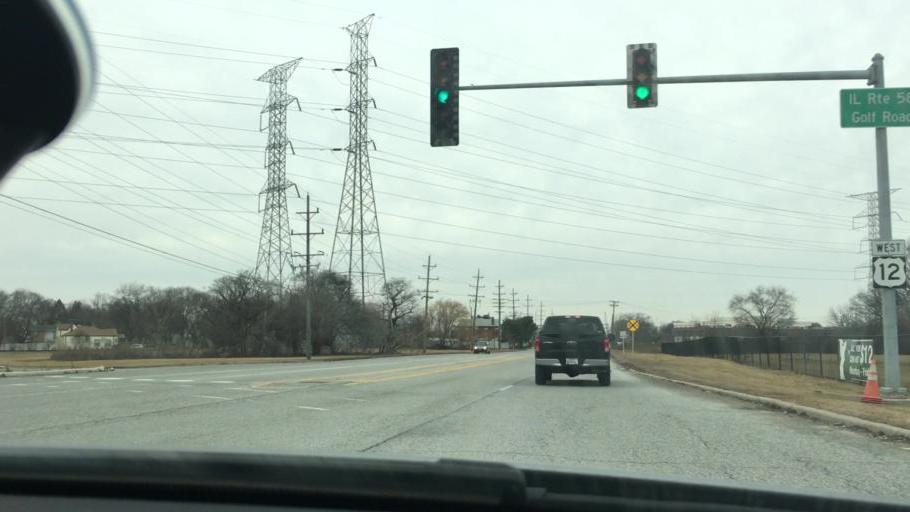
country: US
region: Illinois
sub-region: Cook County
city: Des Plaines
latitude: 42.0543
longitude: -87.8983
